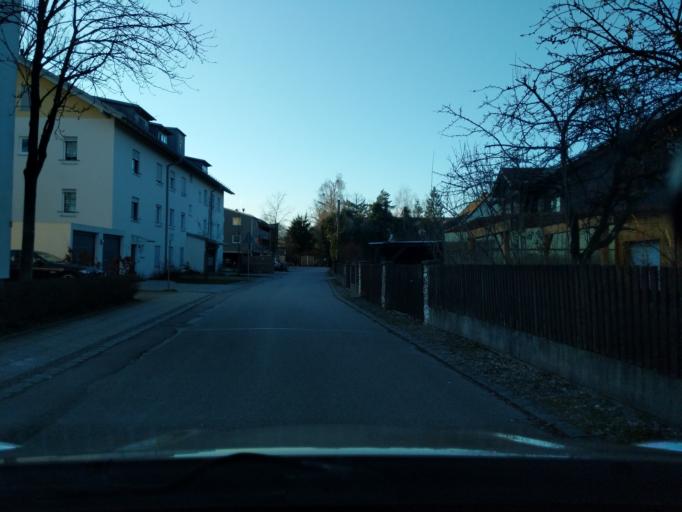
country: DE
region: Bavaria
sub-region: Upper Bavaria
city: Kirchseeon
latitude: 48.0765
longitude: 11.8850
